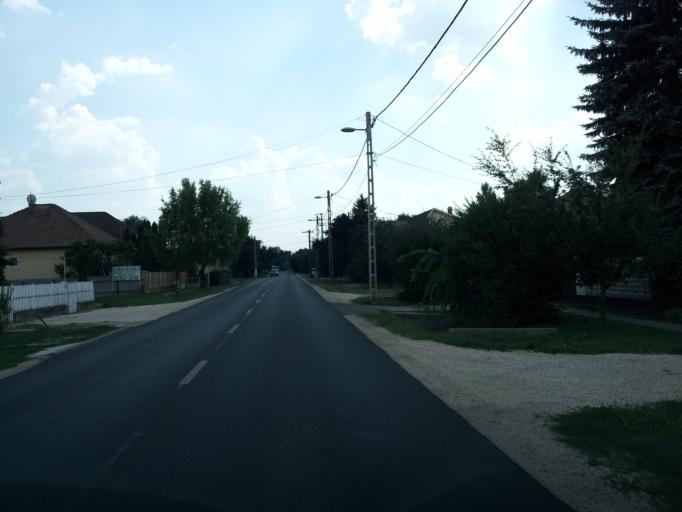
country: HU
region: Pest
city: Toekoel
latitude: 47.3355
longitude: 18.9671
